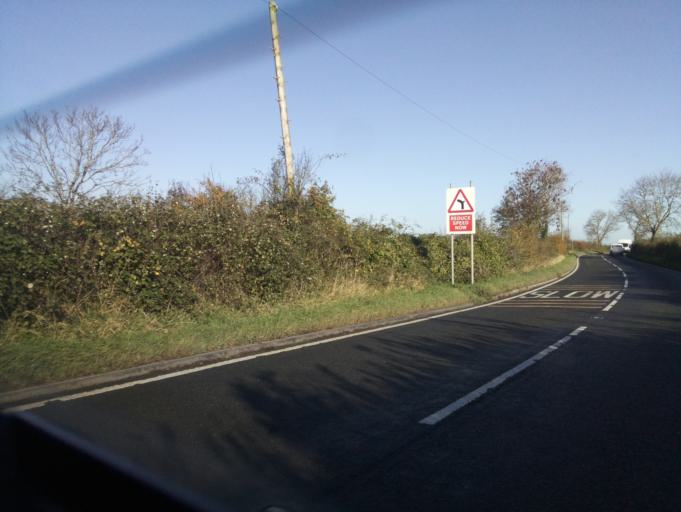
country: GB
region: England
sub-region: Somerset
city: Langport
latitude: 51.0740
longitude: -2.8533
